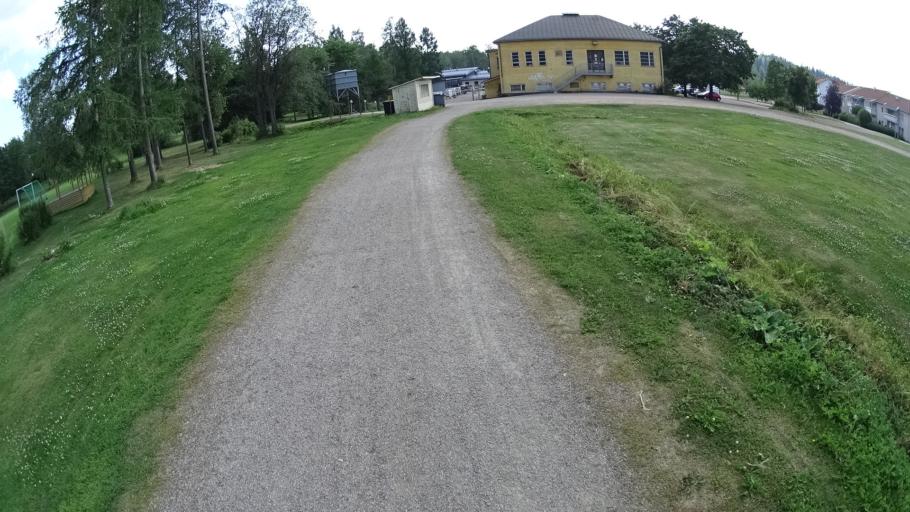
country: FI
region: Uusimaa
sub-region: Porvoo
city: Porvoo
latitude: 60.3863
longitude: 25.6713
